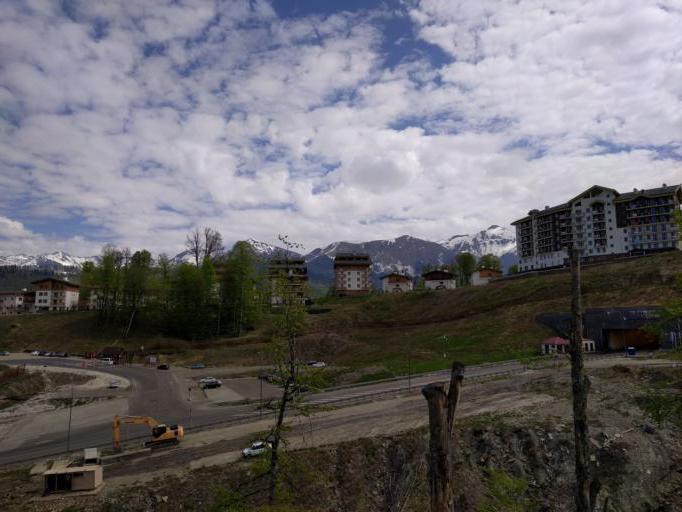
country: RU
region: Krasnodarskiy
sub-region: Sochi City
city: Krasnaya Polyana
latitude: 43.6610
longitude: 40.3152
